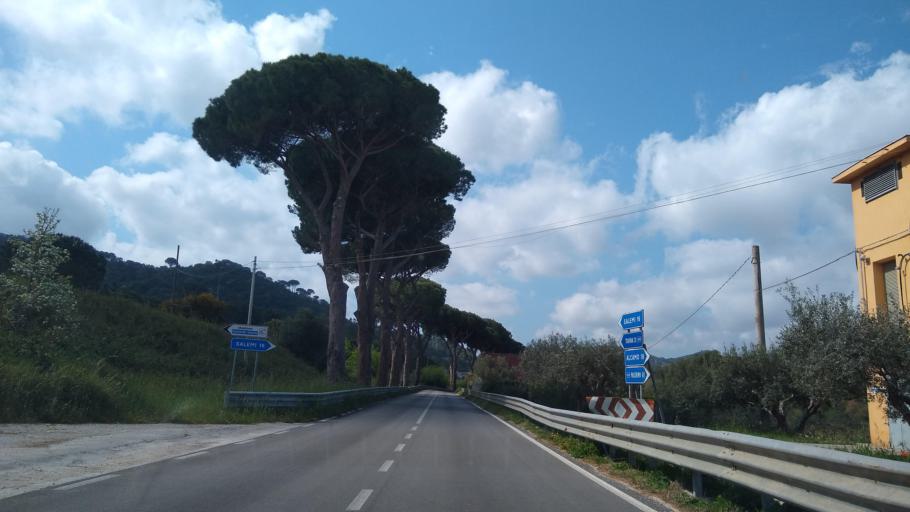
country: IT
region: Sicily
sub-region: Trapani
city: Calatafimi
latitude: 37.9387
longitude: 12.8551
